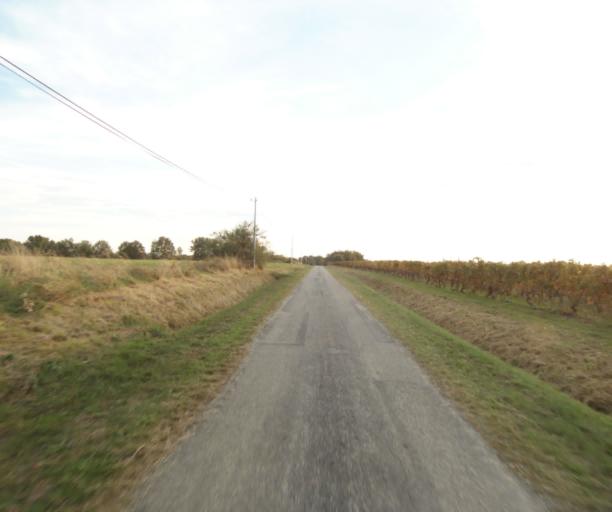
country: FR
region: Midi-Pyrenees
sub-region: Departement du Tarn-et-Garonne
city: Pompignan
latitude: 43.8235
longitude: 1.3238
